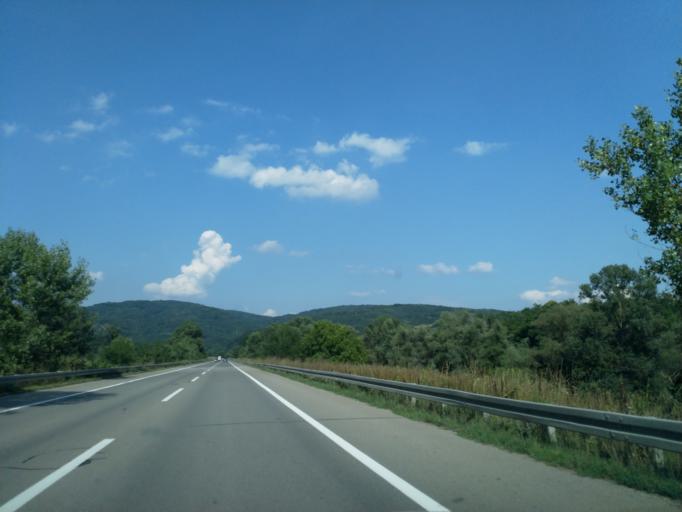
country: RS
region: Central Serbia
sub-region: Rasinski Okrug
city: Krusevac
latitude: 43.6161
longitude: 21.3605
